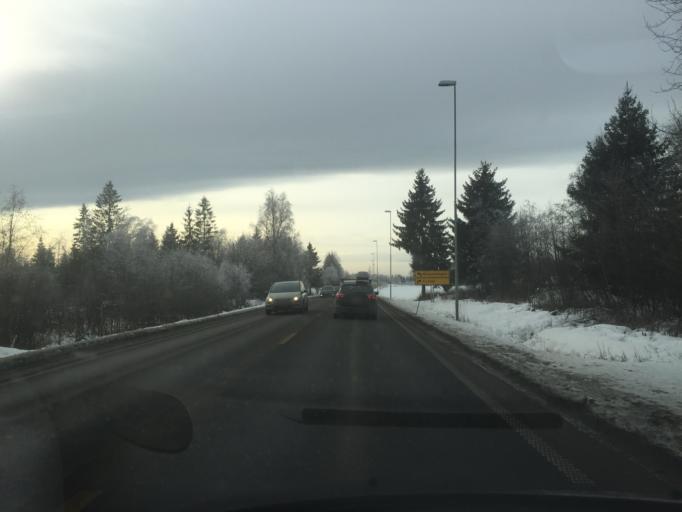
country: NO
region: Hedmark
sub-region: Elverum
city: Elverum
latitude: 60.9290
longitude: 11.6711
